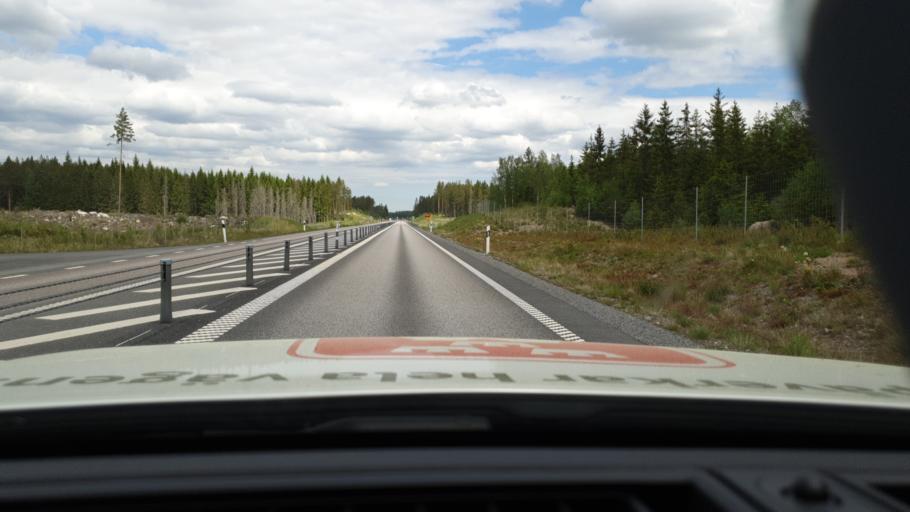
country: SE
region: Uppsala
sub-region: Heby Kommun
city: Tarnsjo
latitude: 60.1001
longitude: 16.9202
